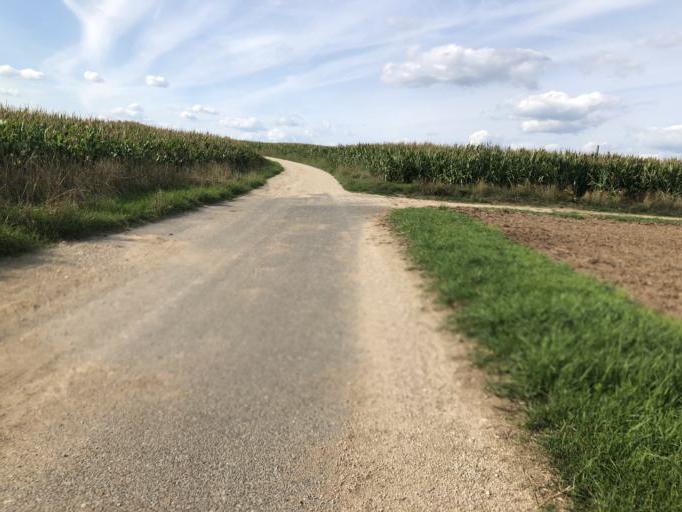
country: DE
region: Bavaria
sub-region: Regierungsbezirk Mittelfranken
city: Erlangen
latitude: 49.5733
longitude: 10.9588
